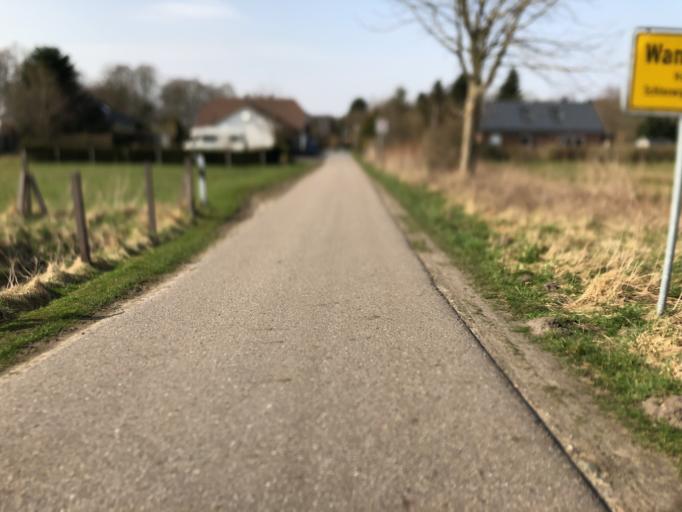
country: DE
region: Schleswig-Holstein
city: Wanderup
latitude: 54.6855
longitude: 9.3371
